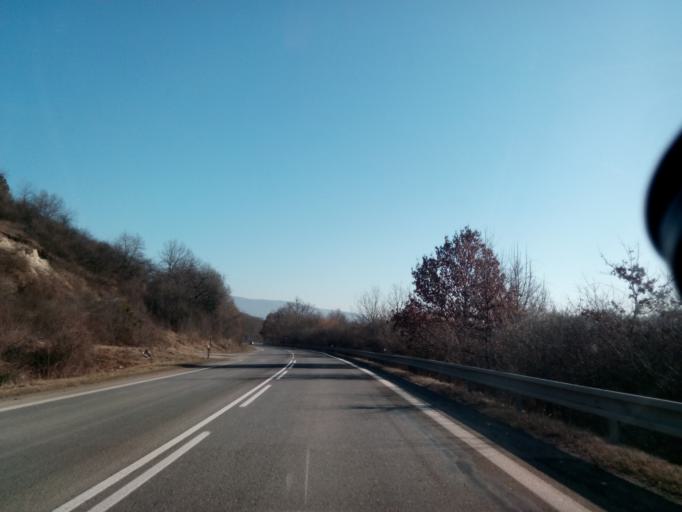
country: SK
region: Kosicky
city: Kosice
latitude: 48.7298
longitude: 21.4488
